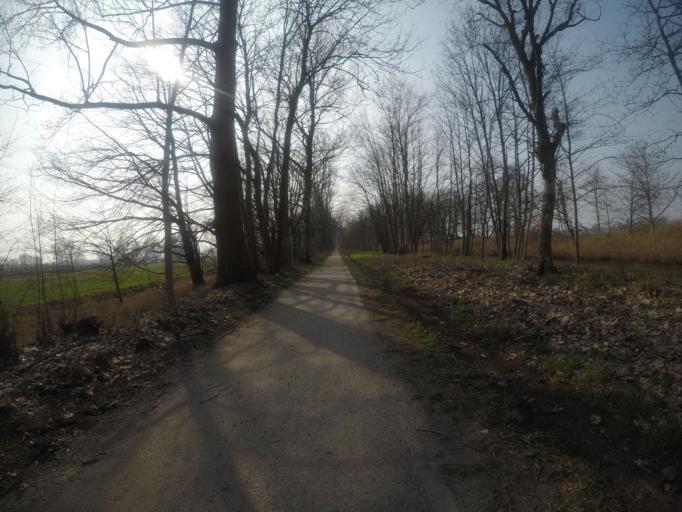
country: DE
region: Brandenburg
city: Mittenwalde
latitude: 52.2844
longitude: 13.5789
